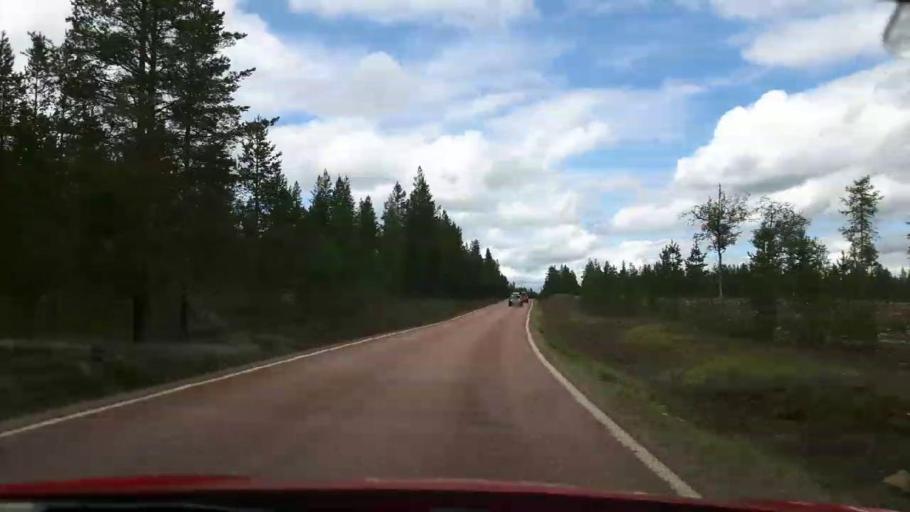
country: NO
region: Hedmark
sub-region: Trysil
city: Innbygda
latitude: 61.8525
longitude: 12.9506
